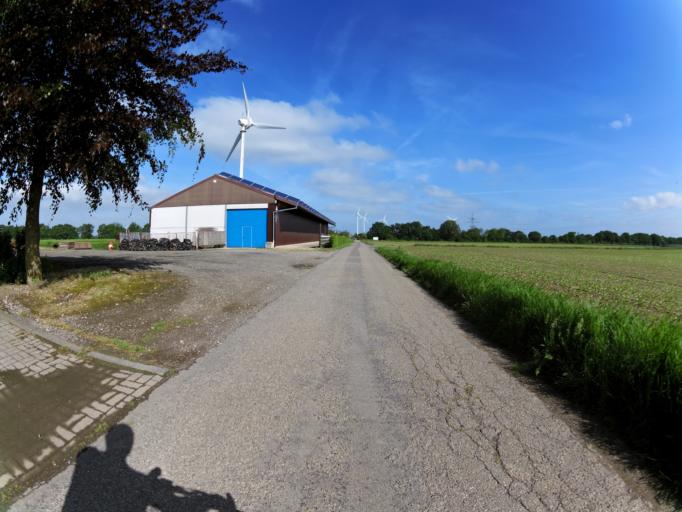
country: DE
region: North Rhine-Westphalia
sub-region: Regierungsbezirk Koln
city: Linnich
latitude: 51.0008
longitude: 6.2248
